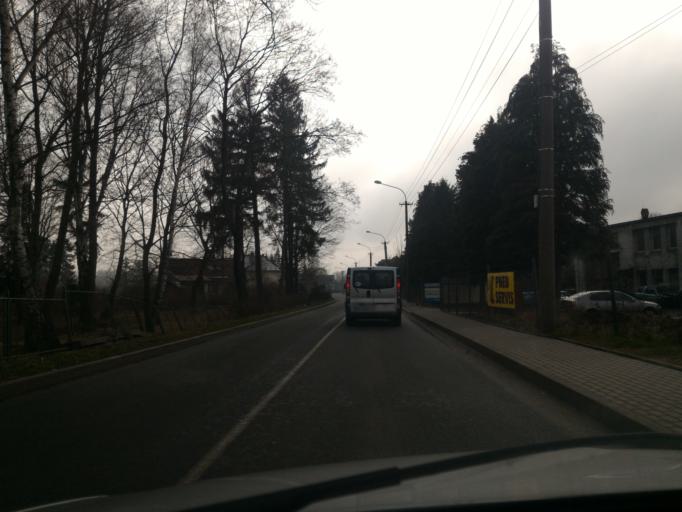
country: CZ
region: Liberecky
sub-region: Okres Liberec
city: Raspenava
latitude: 50.9058
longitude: 15.1110
